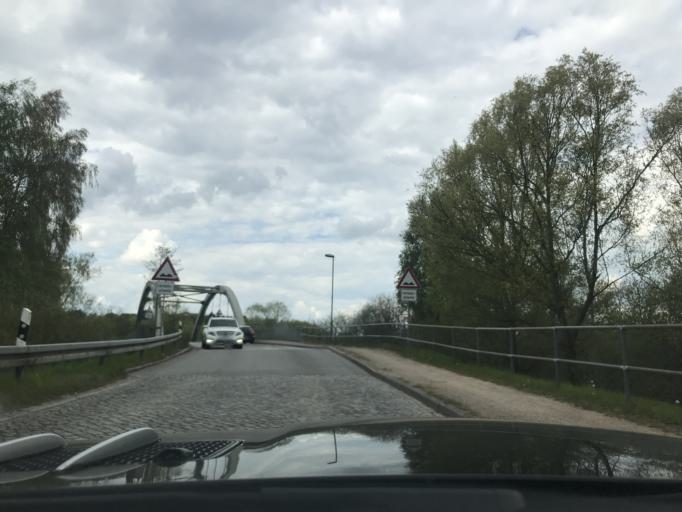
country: DE
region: Schleswig-Holstein
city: Gross Gronau
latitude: 53.7821
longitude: 10.7679
